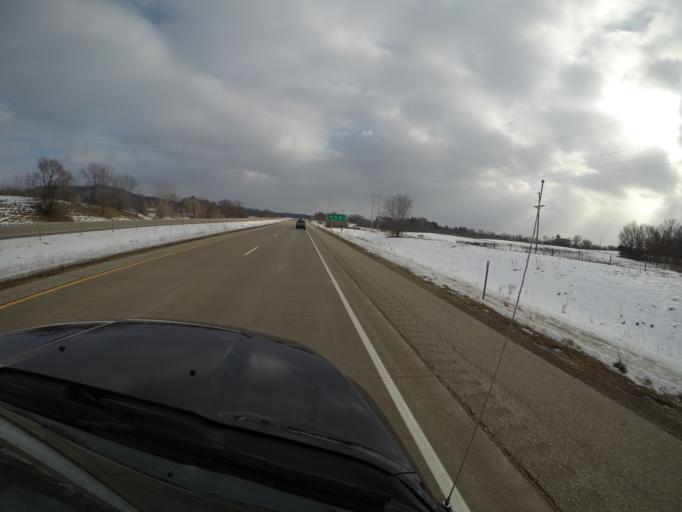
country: US
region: Wisconsin
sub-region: La Crosse County
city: Holmen
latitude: 43.9460
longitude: -91.2642
